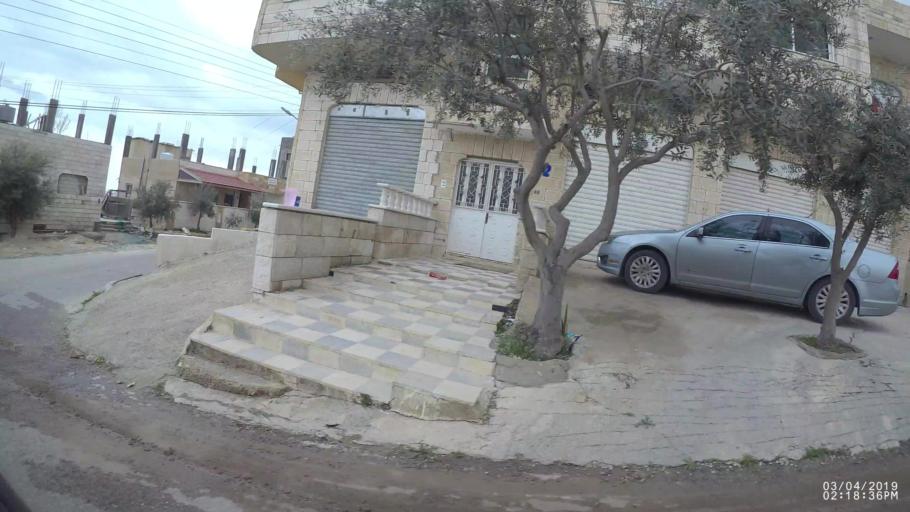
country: JO
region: Amman
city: Wadi as Sir
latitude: 31.9400
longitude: 35.8324
